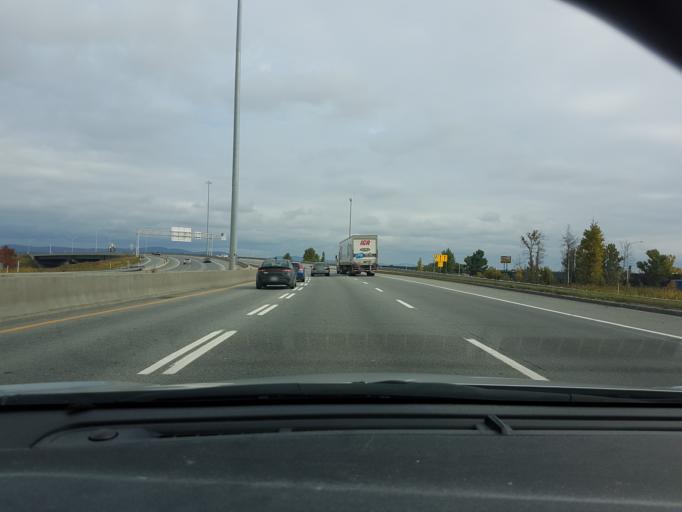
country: CA
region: Quebec
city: L'Ancienne-Lorette
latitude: 46.7977
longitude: -71.2868
